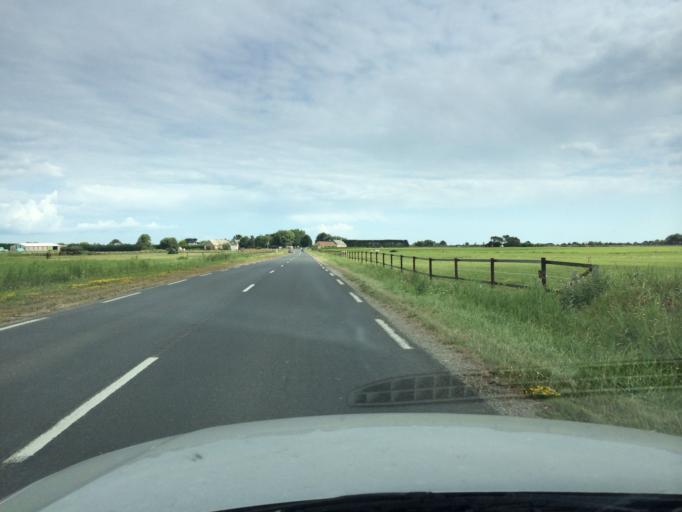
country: FR
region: Lower Normandy
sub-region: Departement de la Manche
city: Saint-Hilaire-Petitville
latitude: 49.4087
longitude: -1.1894
